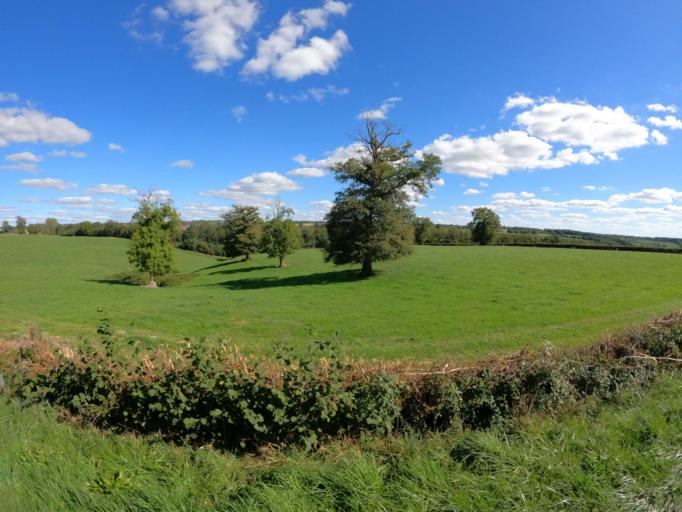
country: FR
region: Auvergne
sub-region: Departement de l'Allier
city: Buxieres-les-Mines
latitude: 46.4013
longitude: 2.8934
